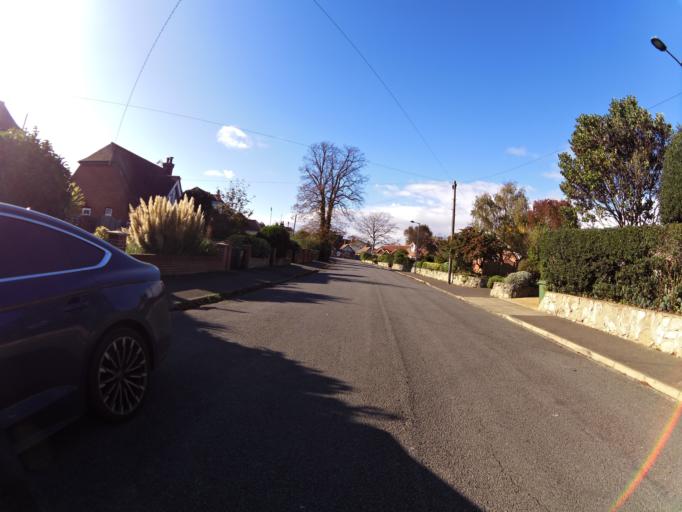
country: GB
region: England
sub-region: Suffolk
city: Felixstowe
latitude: 51.9670
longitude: 1.3571
